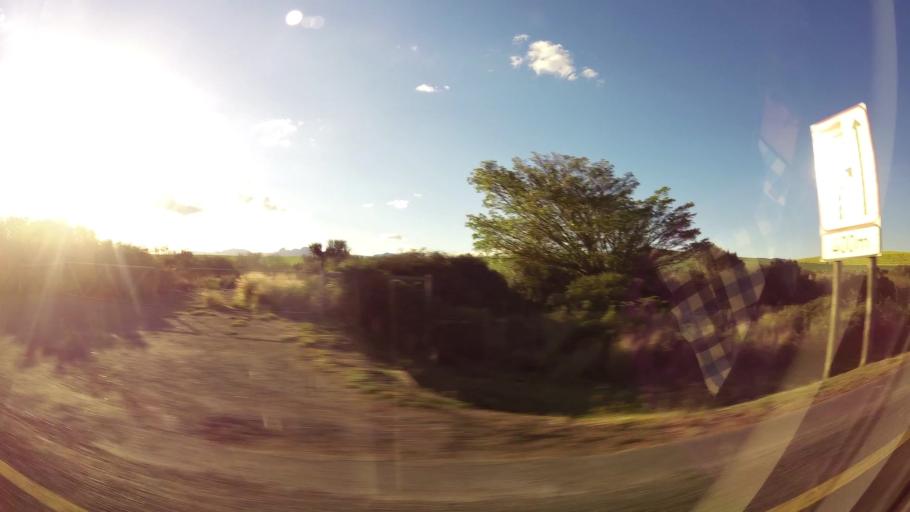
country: ZA
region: Western Cape
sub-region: Eden District Municipality
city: Riversdale
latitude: -34.0861
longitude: 20.9841
